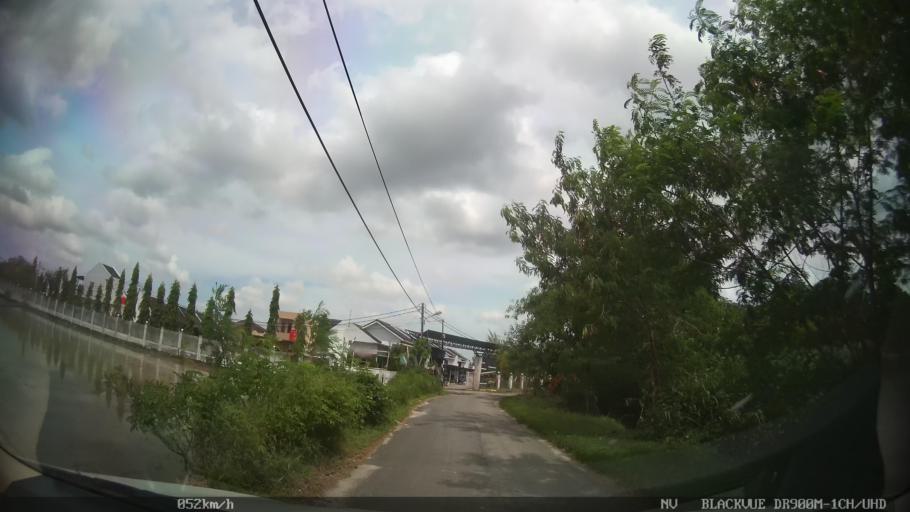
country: ID
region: North Sumatra
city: Percut
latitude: 3.5659
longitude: 98.8557
